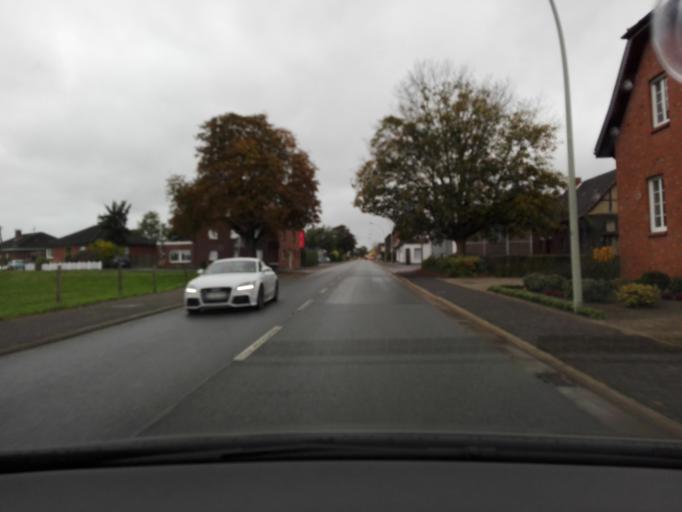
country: DE
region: North Rhine-Westphalia
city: Selm
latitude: 51.6644
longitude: 7.4839
